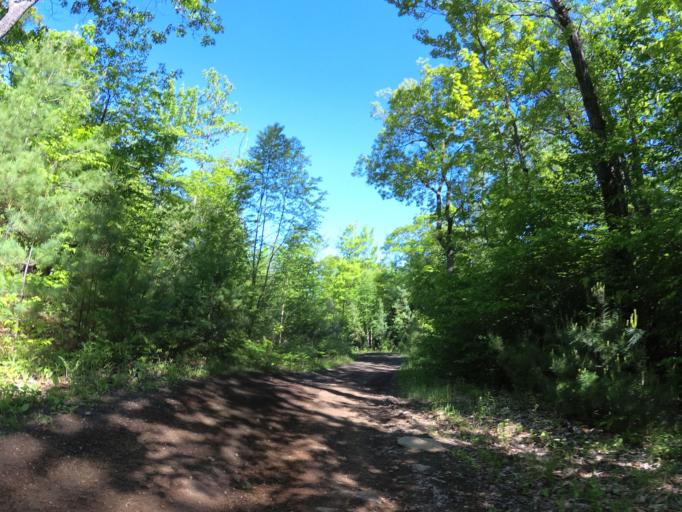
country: CA
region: Ontario
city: Renfrew
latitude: 45.0969
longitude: -77.0655
